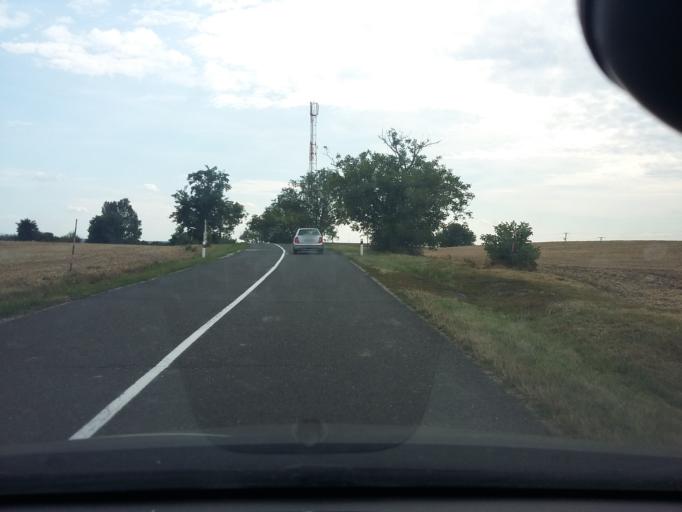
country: SK
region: Trnavsky
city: Gbely
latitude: 48.6636
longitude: 17.1461
